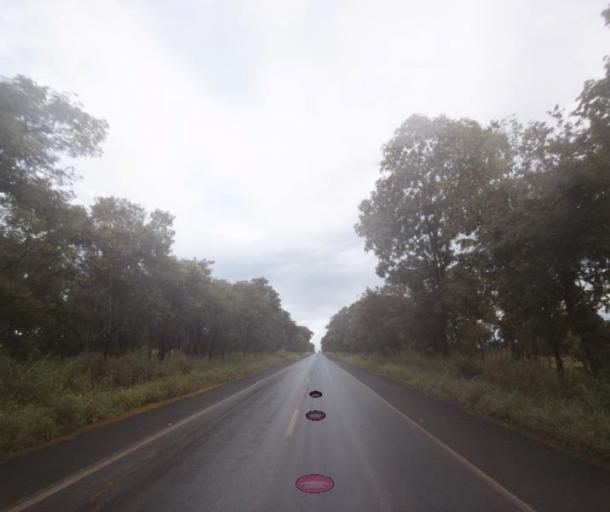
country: BR
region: Goias
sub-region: Porangatu
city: Porangatu
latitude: -13.7910
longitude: -49.0348
